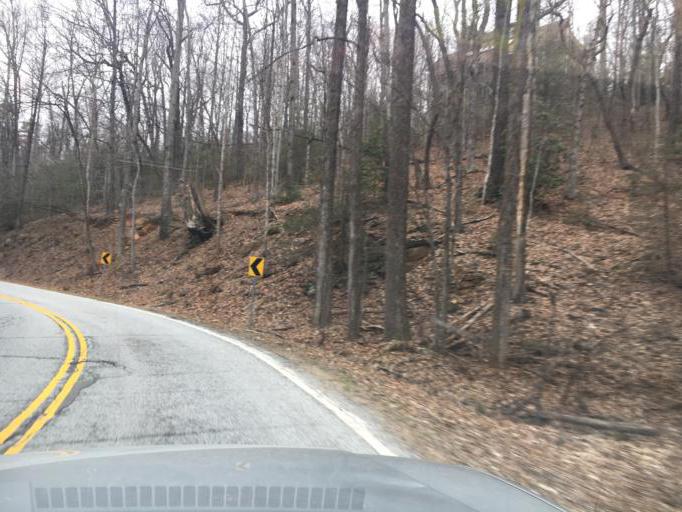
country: US
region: South Carolina
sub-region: Greenville County
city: Slater-Marietta
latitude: 35.1064
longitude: -82.6075
